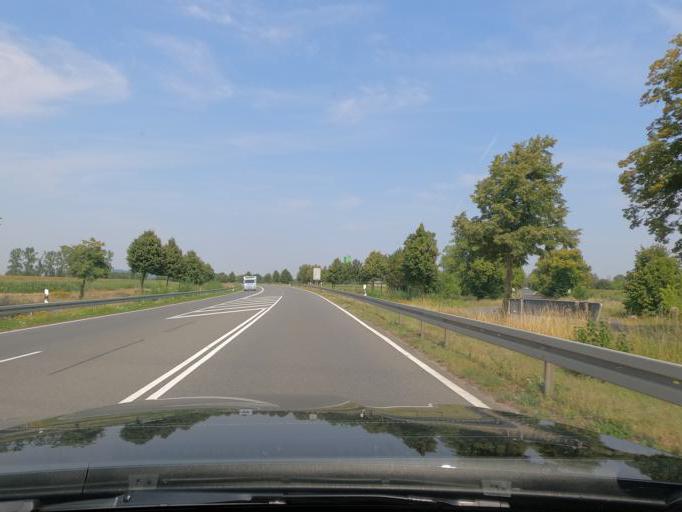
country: DE
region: Lower Saxony
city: Gehrden
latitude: 52.2878
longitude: 9.6300
